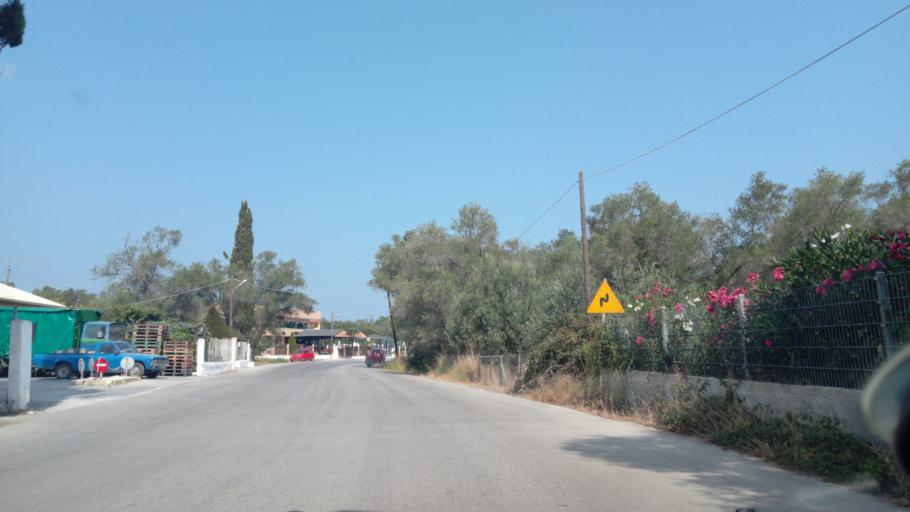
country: GR
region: Ionian Islands
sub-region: Nomos Kerkyras
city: Lefkimmi
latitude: 39.4080
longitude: 20.0936
